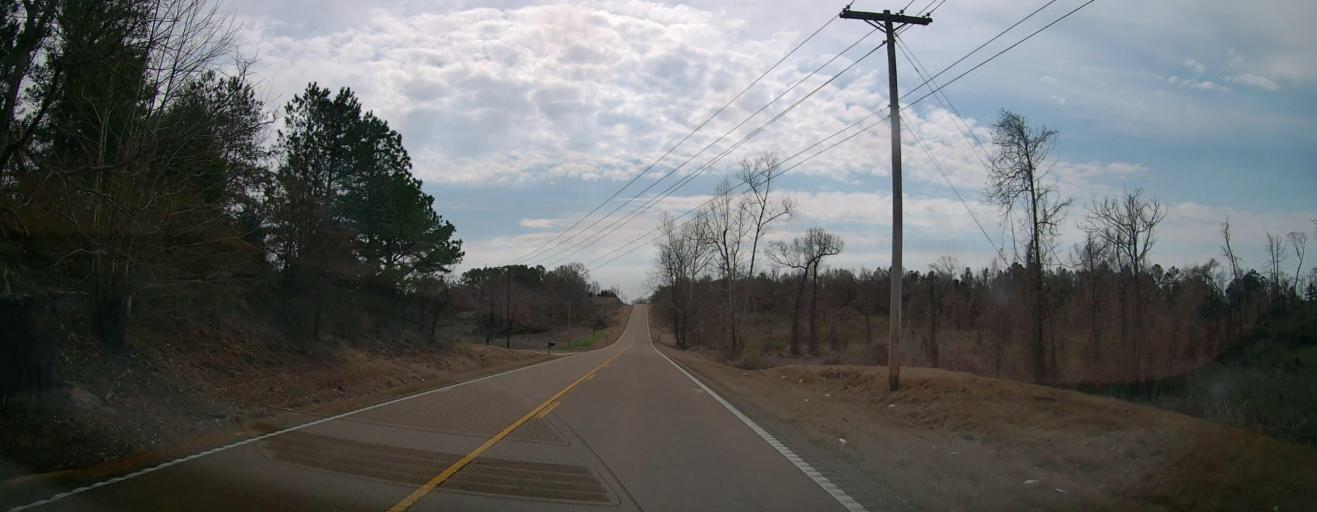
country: US
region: Mississippi
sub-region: Marshall County
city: Holly Springs
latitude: 34.7435
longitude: -89.4260
